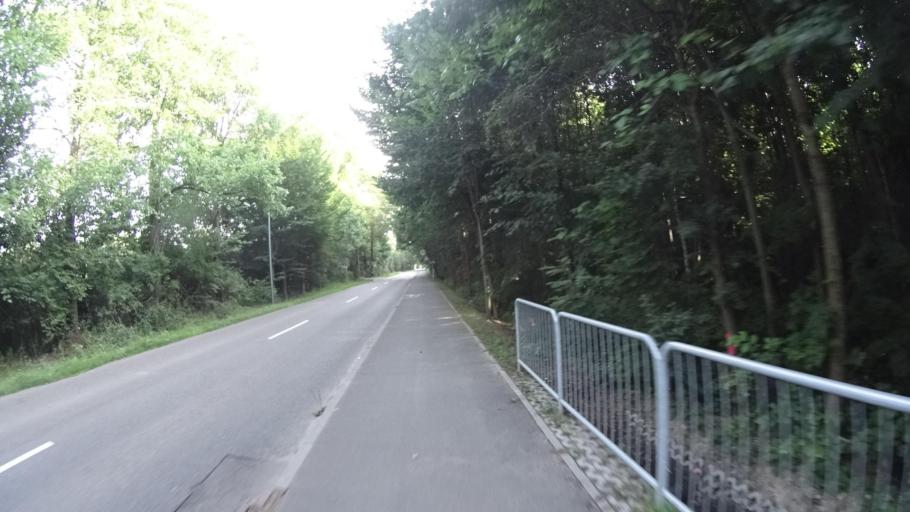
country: PL
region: Masovian Voivodeship
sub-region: Powiat pruszkowski
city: Nadarzyn
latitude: 52.0380
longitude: 20.7822
